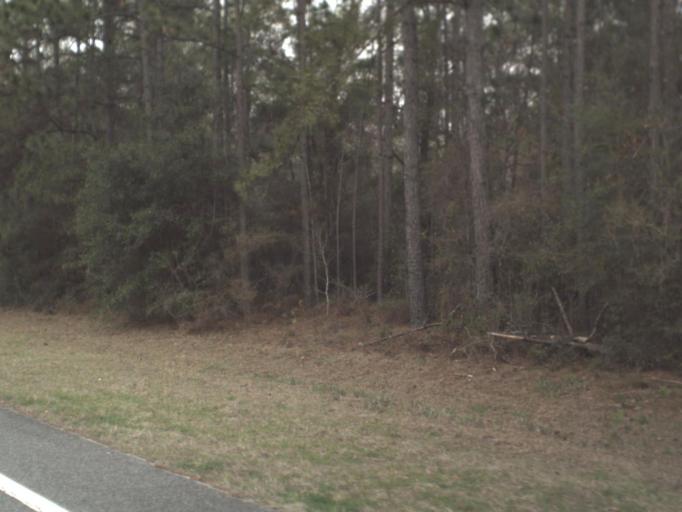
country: US
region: Florida
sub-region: Wakulla County
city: Crawfordville
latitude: 30.1675
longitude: -84.2497
